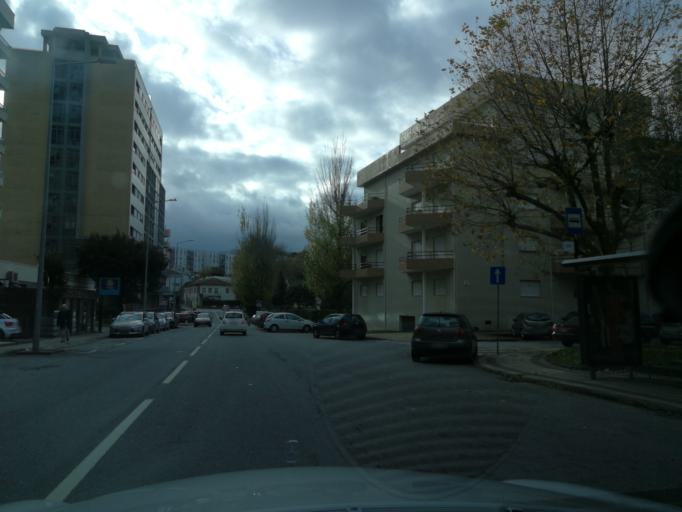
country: PT
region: Braga
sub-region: Braga
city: Braga
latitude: 41.5489
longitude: -8.4102
